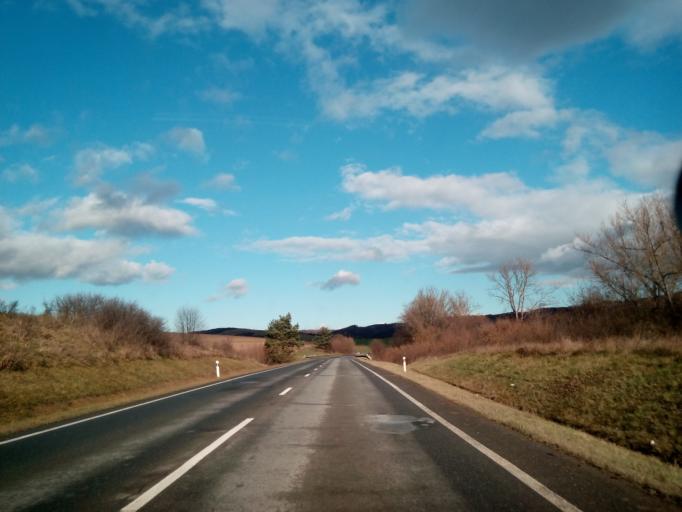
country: SK
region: Presovsky
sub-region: Okres Bardejov
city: Bardejov
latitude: 49.1943
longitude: 21.3091
